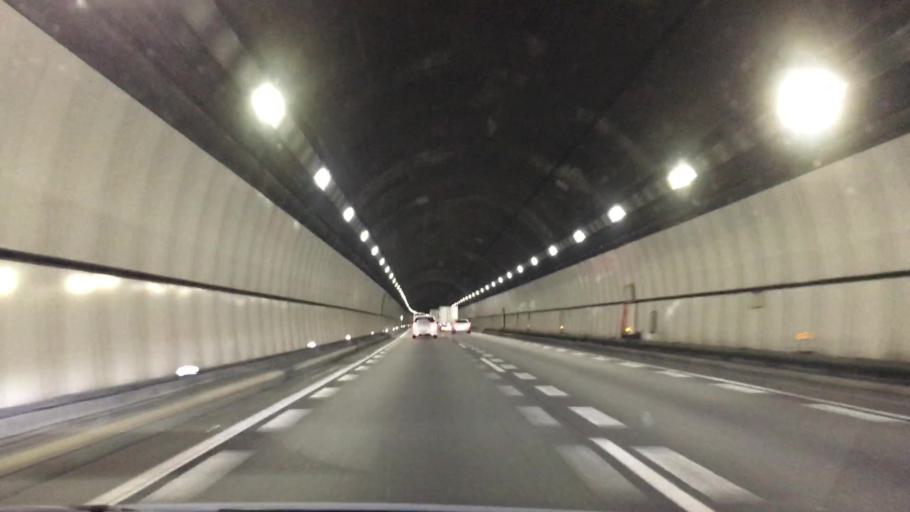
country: JP
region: Shizuoka
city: Shizuoka-shi
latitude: 35.0586
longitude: 138.5200
